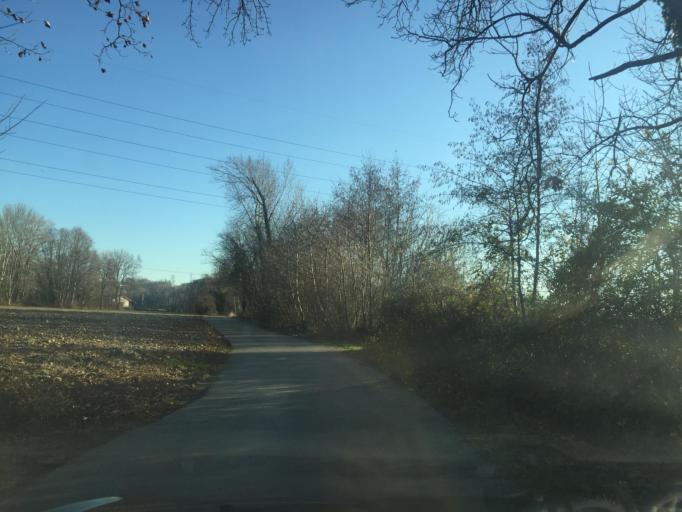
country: IT
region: Friuli Venezia Giulia
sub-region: Provincia di Udine
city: Buia
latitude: 46.2414
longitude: 13.1117
